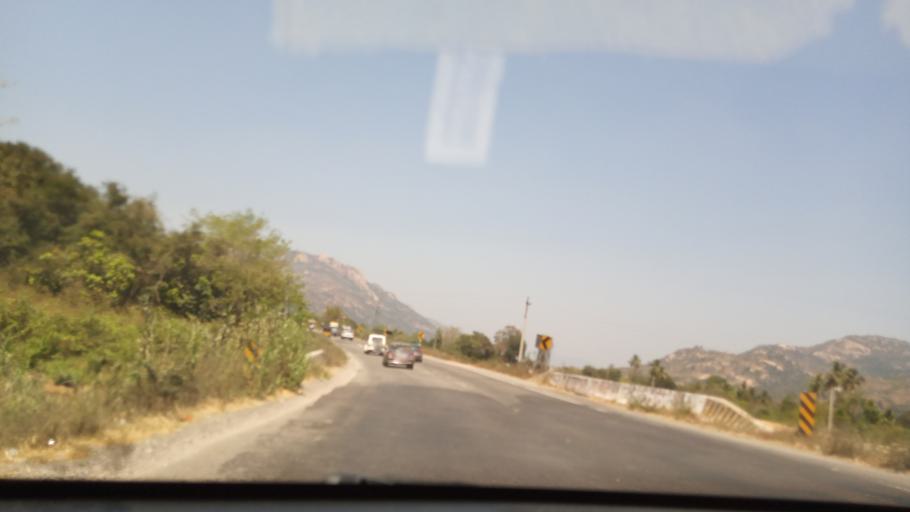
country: IN
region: Andhra Pradesh
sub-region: Chittoor
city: Pakala
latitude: 13.4918
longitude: 79.2026
